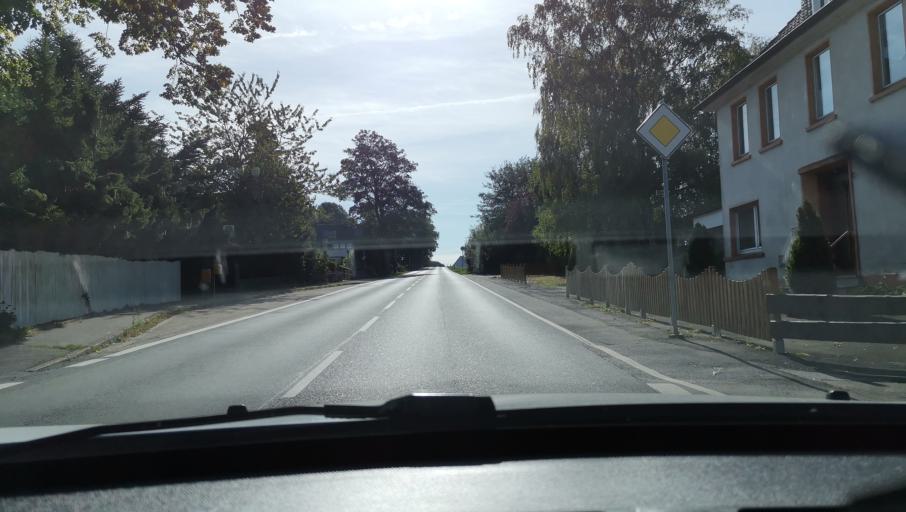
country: DE
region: North Rhine-Westphalia
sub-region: Regierungsbezirk Arnsberg
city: Breckerfeld
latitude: 51.2769
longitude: 7.4405
